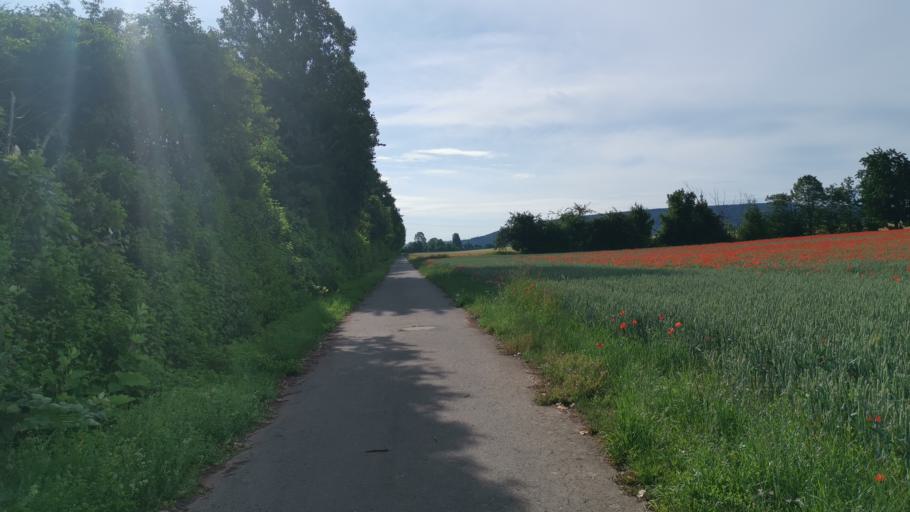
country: DE
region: Rheinland-Pfalz
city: Mandel
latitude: 49.8555
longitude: 7.7890
